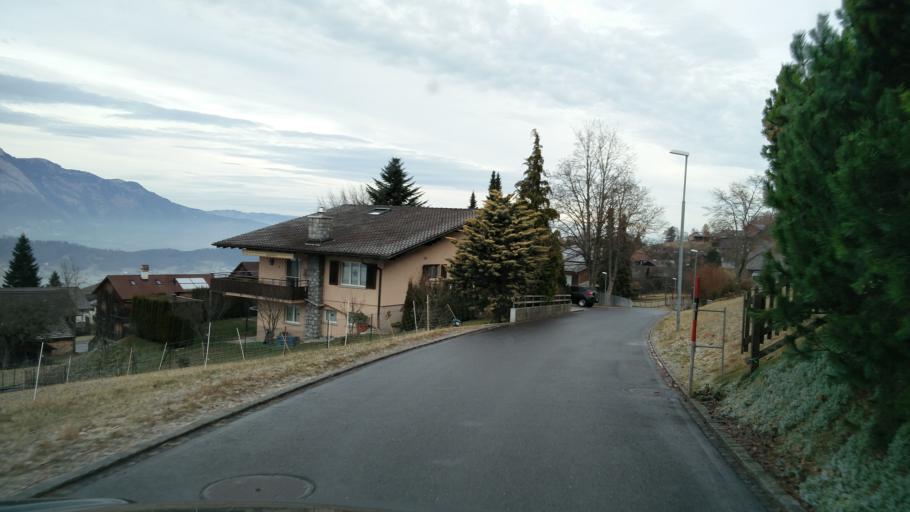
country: LI
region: Planken
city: Planken
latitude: 47.1846
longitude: 9.5459
